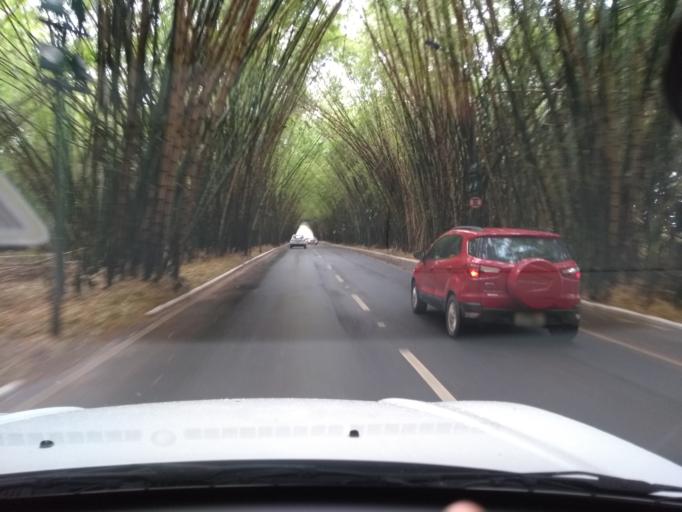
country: BR
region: Bahia
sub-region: Lauro De Freitas
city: Lauro de Freitas
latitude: -12.9077
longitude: -38.3412
